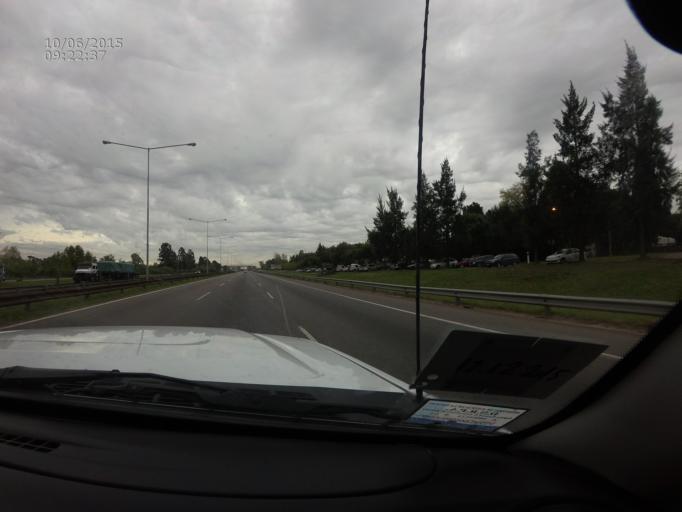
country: AR
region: Buenos Aires
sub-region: Partido de Campana
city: Campana
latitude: -34.2169
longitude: -58.9250
